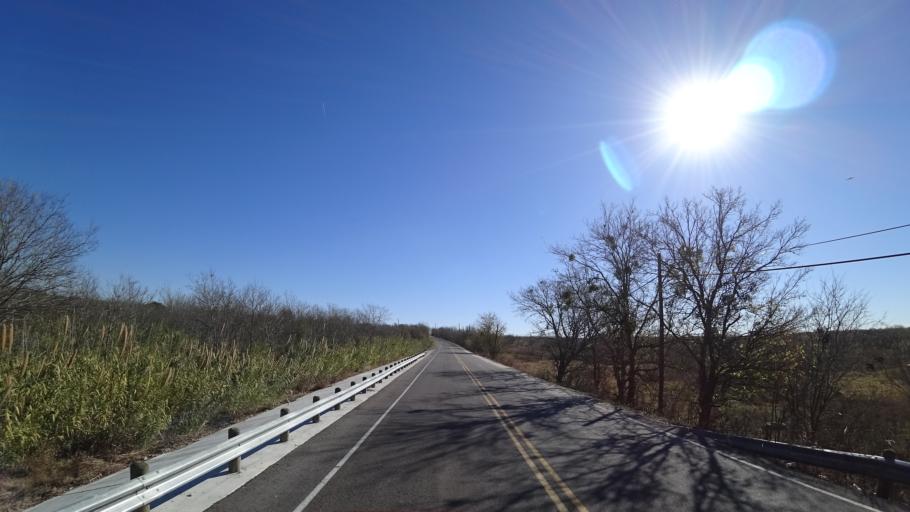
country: US
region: Texas
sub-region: Travis County
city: Garfield
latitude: 30.1161
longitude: -97.6571
